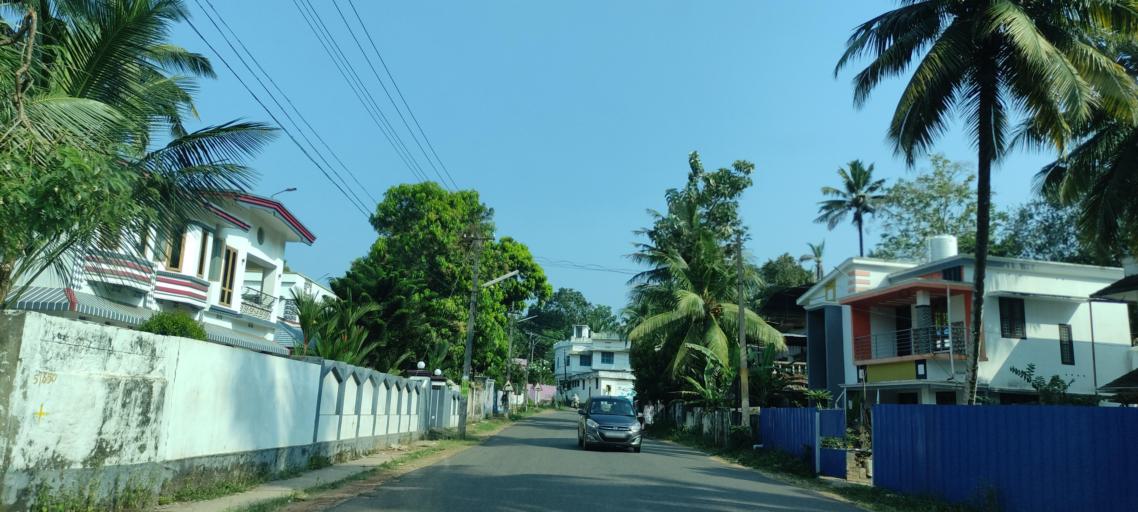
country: IN
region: Kerala
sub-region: Kollam
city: Panmana
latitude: 9.0444
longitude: 76.5788
